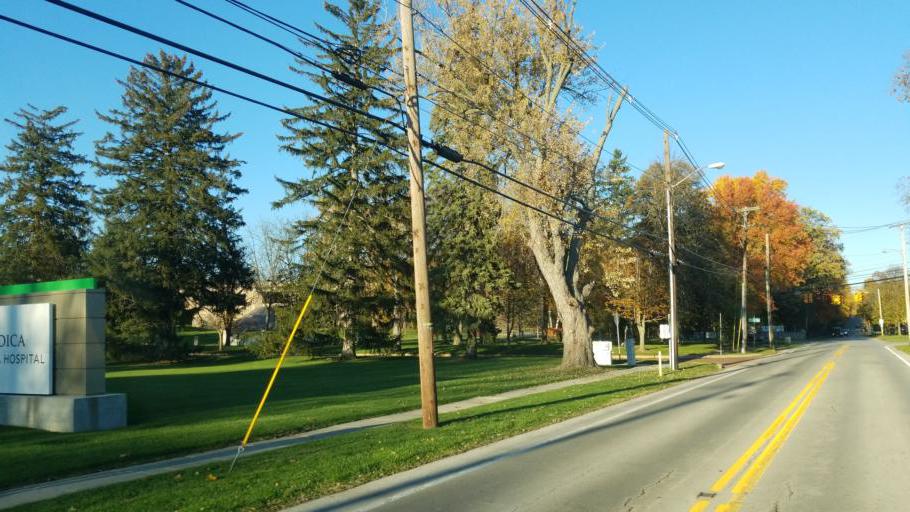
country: US
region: Ohio
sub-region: Sandusky County
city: Ballville
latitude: 41.3376
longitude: -83.1332
